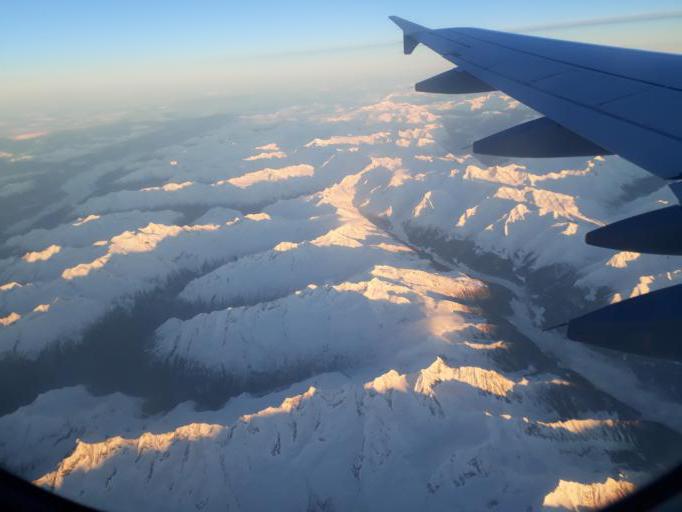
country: AT
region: Tyrol
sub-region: Politischer Bezirk Schwaz
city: Mayrhofen
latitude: 47.0500
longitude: 11.8641
